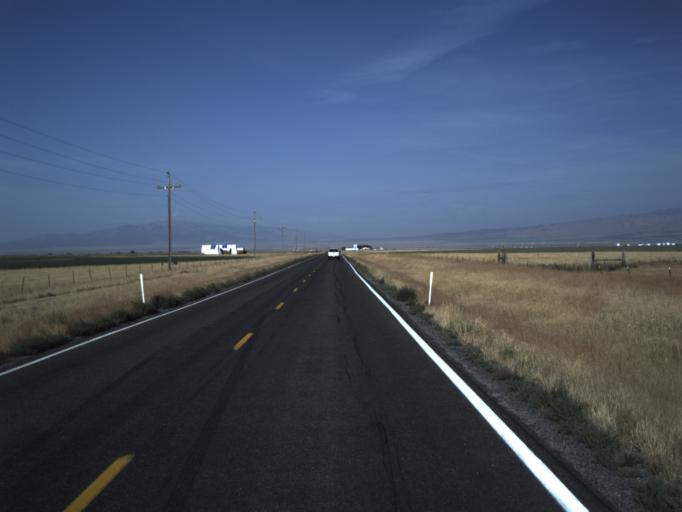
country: US
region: Idaho
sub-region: Oneida County
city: Malad City
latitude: 41.9664
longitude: -112.7763
